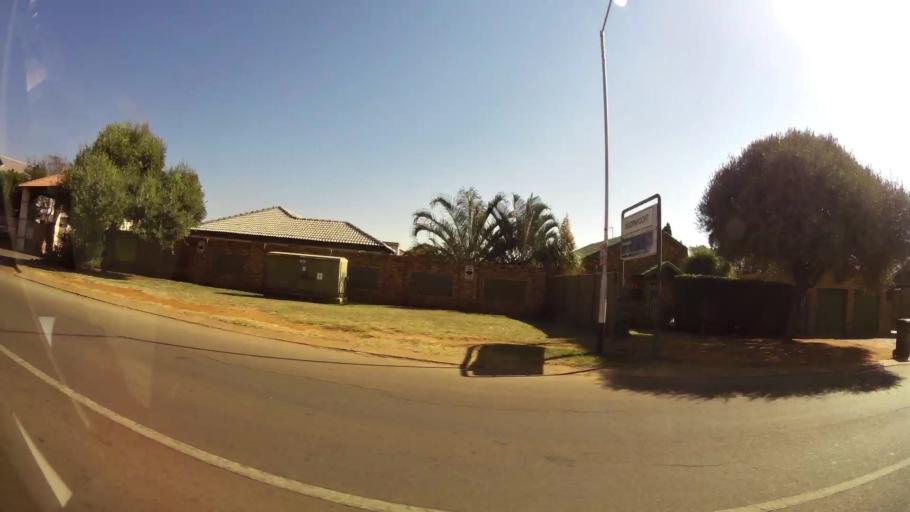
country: ZA
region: Gauteng
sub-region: City of Tshwane Metropolitan Municipality
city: Pretoria
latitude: -25.6589
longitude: 28.2504
